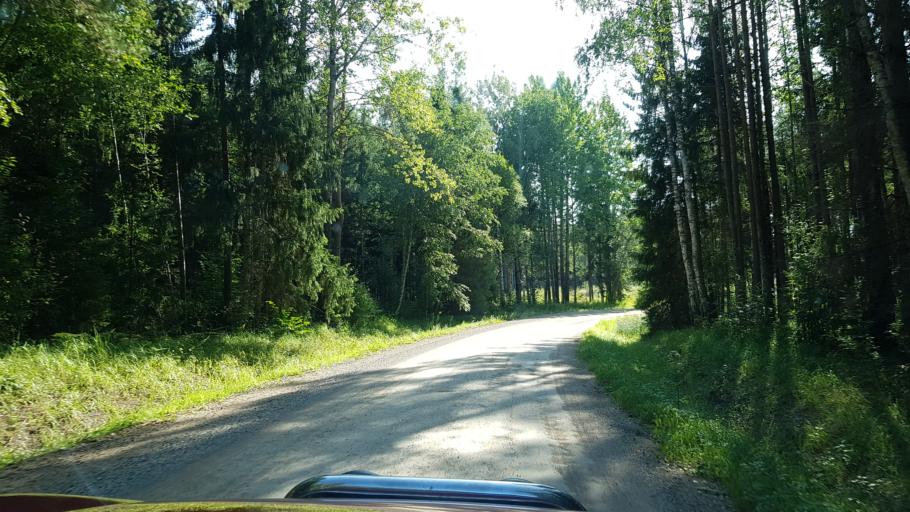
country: LV
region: Apes Novads
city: Ape
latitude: 57.6151
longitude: 26.8167
